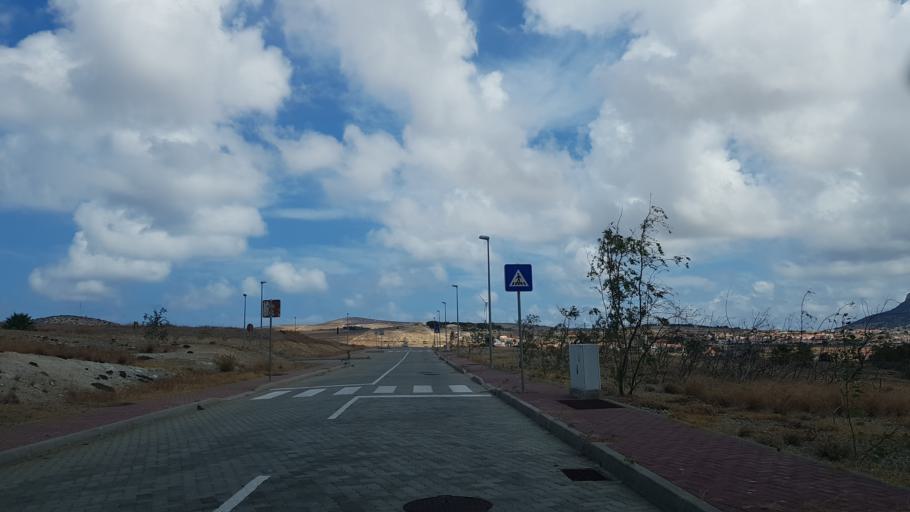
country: PT
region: Madeira
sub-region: Porto Santo
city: Vila de Porto Santo
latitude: 33.0486
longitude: -16.3630
